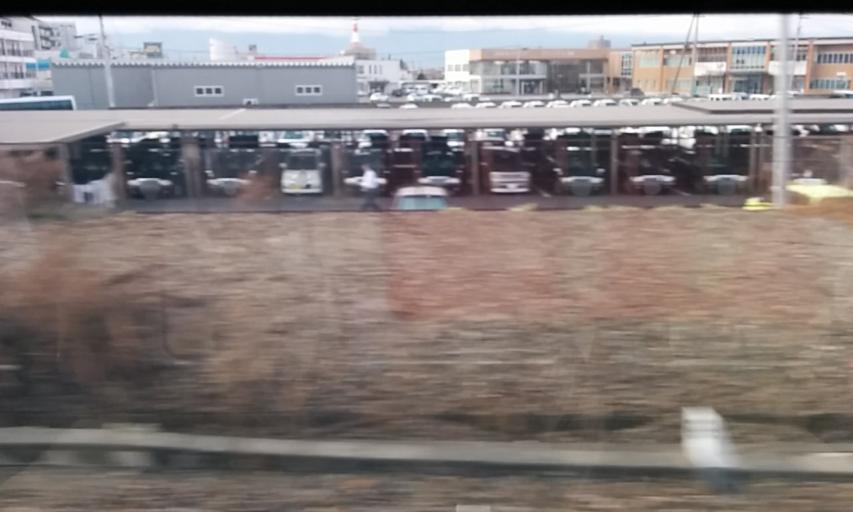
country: JP
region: Nagano
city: Matsumoto
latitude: 36.2144
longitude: 137.9710
